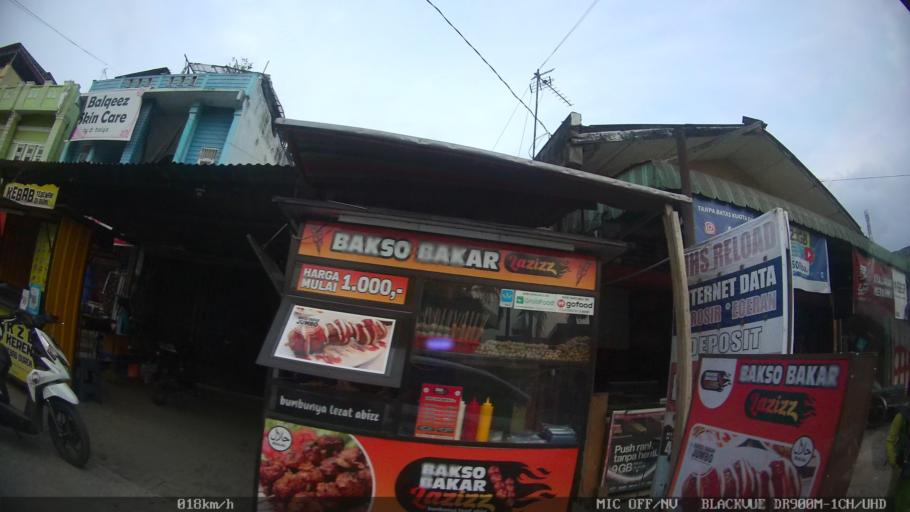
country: ID
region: North Sumatra
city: Sunggal
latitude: 3.5885
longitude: 98.6010
